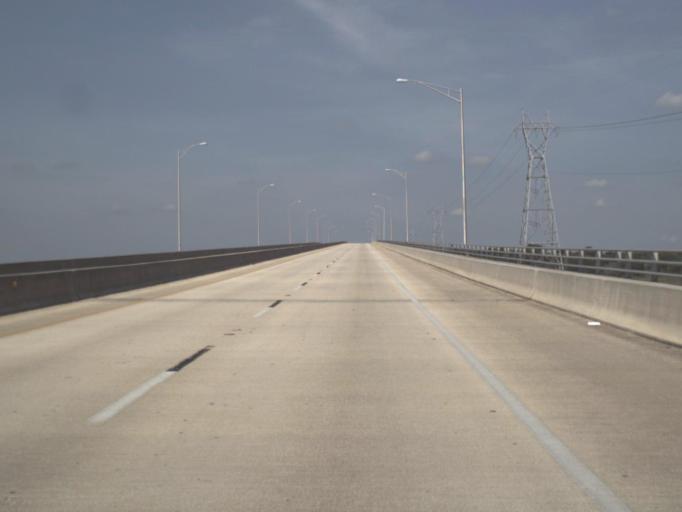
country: US
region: Florida
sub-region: Duval County
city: Atlantic Beach
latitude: 30.3632
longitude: -81.4368
